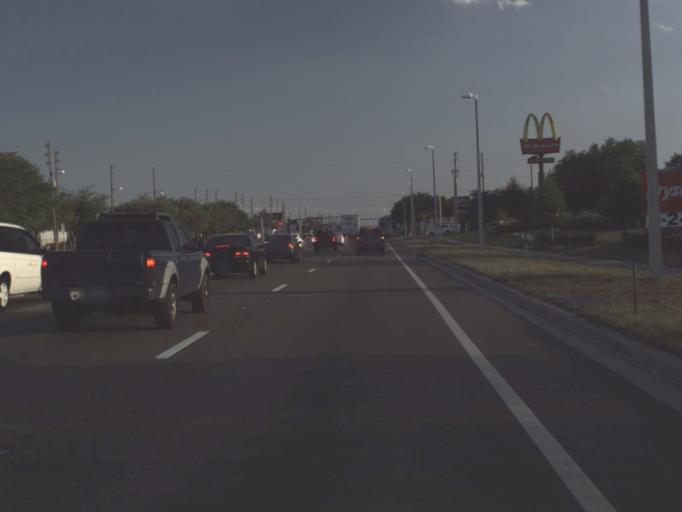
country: US
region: Florida
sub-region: Orange County
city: Southchase
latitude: 28.4009
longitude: -81.4047
